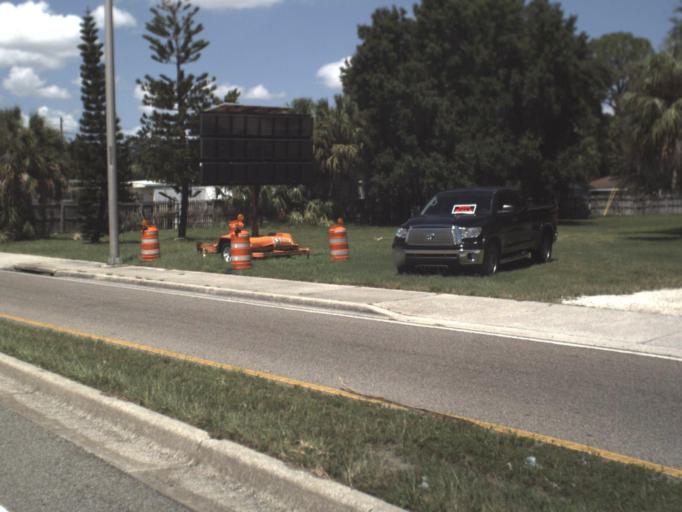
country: US
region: Florida
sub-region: Pinellas County
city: Pinellas Park
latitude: 27.8394
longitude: -82.6864
